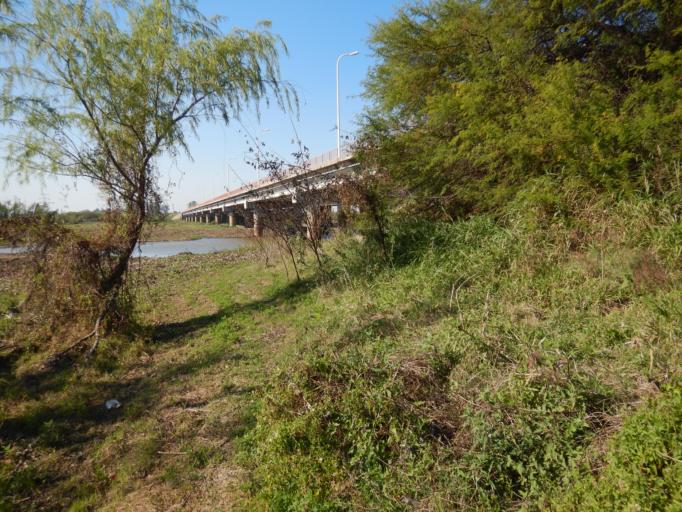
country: AR
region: Entre Rios
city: Parana
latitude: -31.6708
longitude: -60.5795
